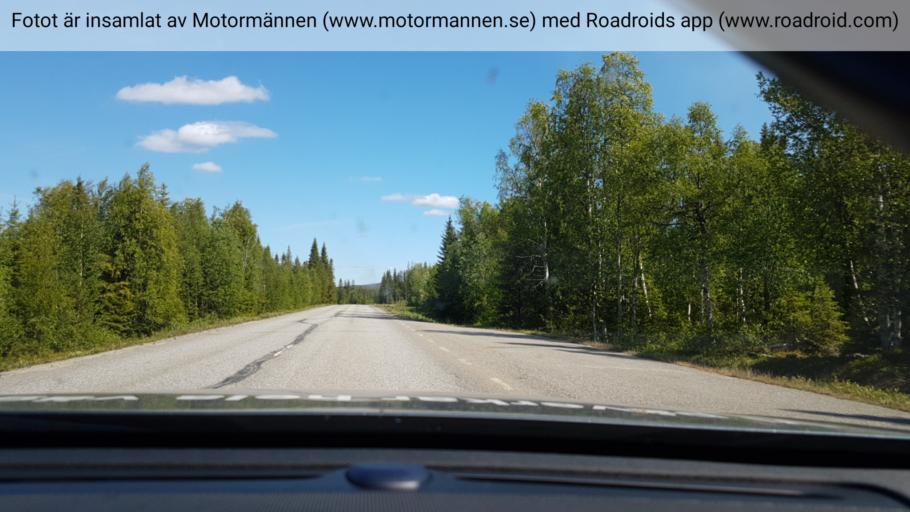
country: SE
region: Vaesterbotten
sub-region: Lycksele Kommun
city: Soderfors
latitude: 64.6347
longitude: 17.9125
